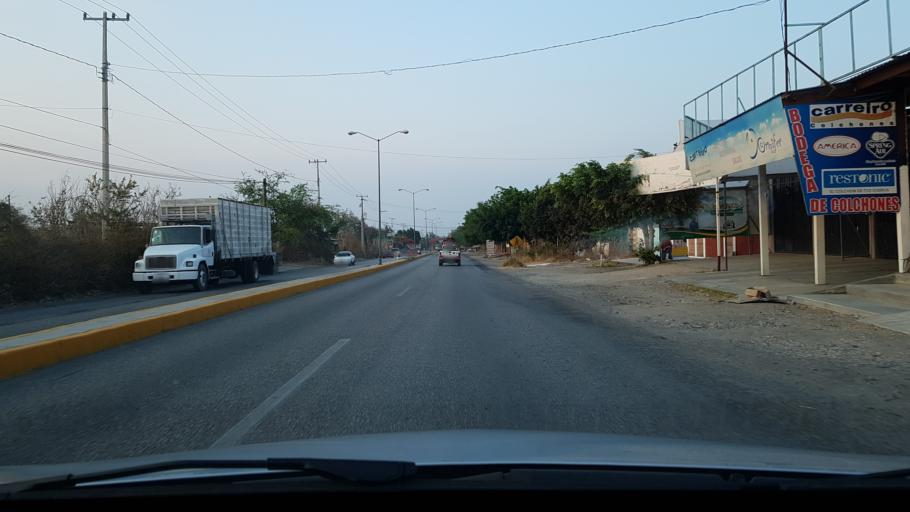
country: MX
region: Morelos
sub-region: Jonacatepec
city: Amacuitlapilco
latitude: 18.7043
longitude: -98.8006
